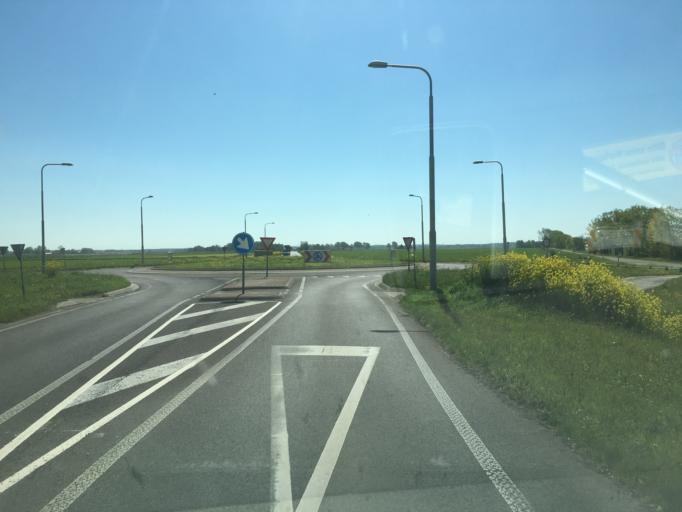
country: NL
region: Friesland
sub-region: Sudwest Fryslan
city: Koudum
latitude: 52.8967
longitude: 5.4683
